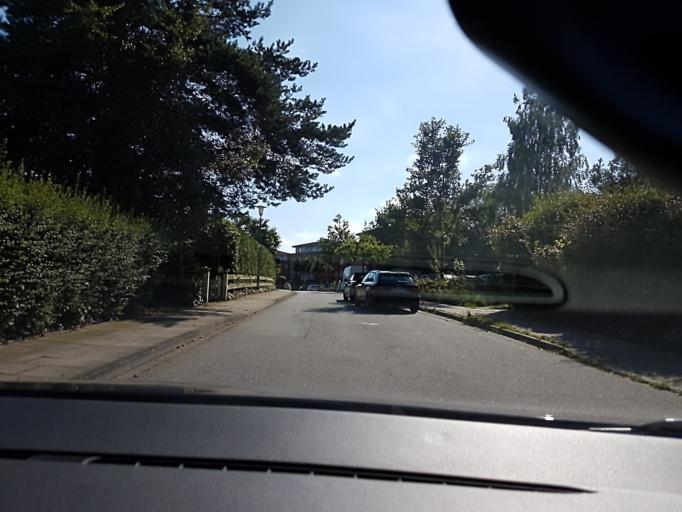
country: DE
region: Schleswig-Holstein
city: Scharbeutz
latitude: 54.0522
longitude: 10.7421
